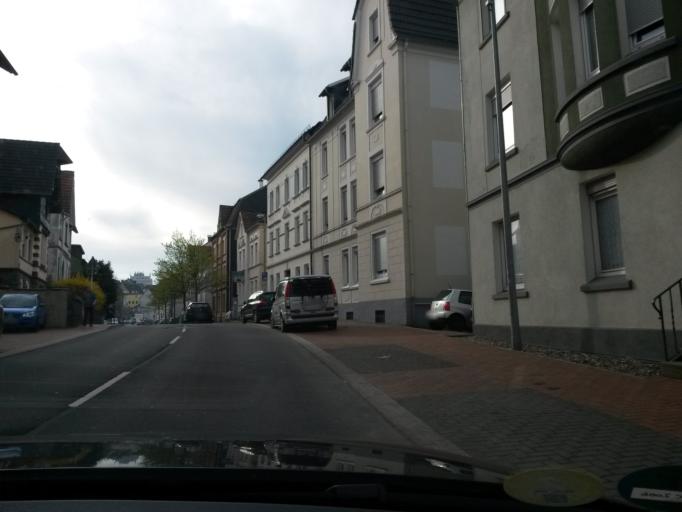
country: DE
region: North Rhine-Westphalia
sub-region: Regierungsbezirk Arnsberg
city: Luedenscheid
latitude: 51.2186
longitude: 7.6227
